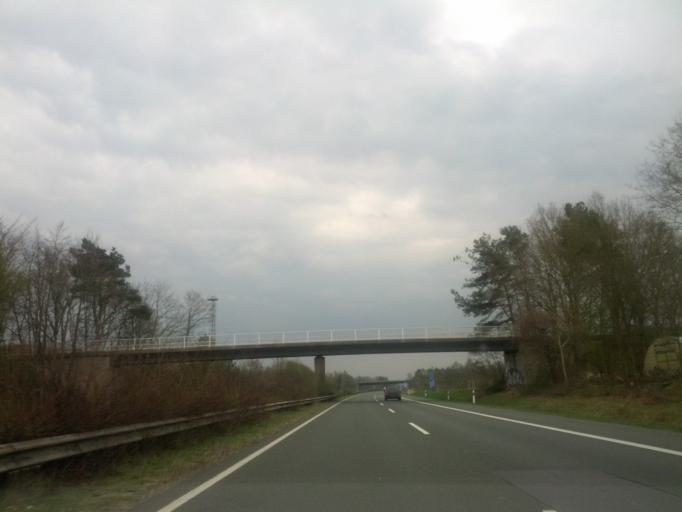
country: DE
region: Lower Saxony
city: Wiefelstede
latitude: 53.1937
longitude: 8.0990
